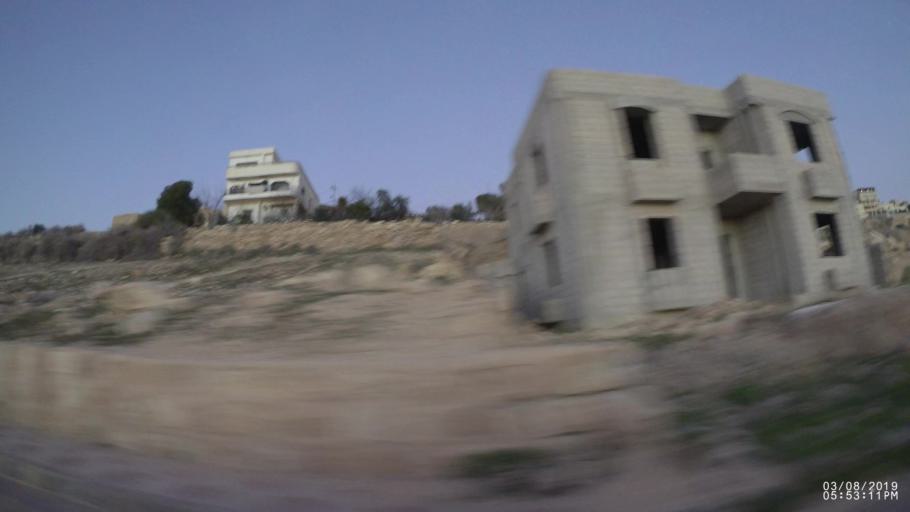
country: JO
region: Ma'an
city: Petra
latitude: 30.3232
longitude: 35.4812
